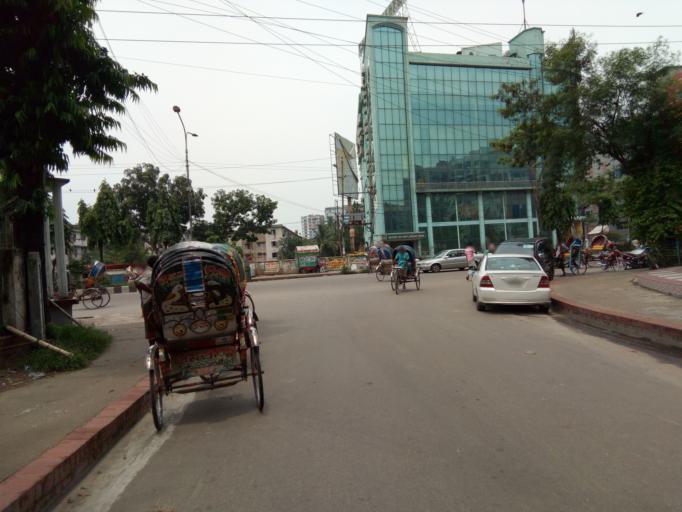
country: BD
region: Dhaka
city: Azimpur
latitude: 23.7455
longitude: 90.3810
